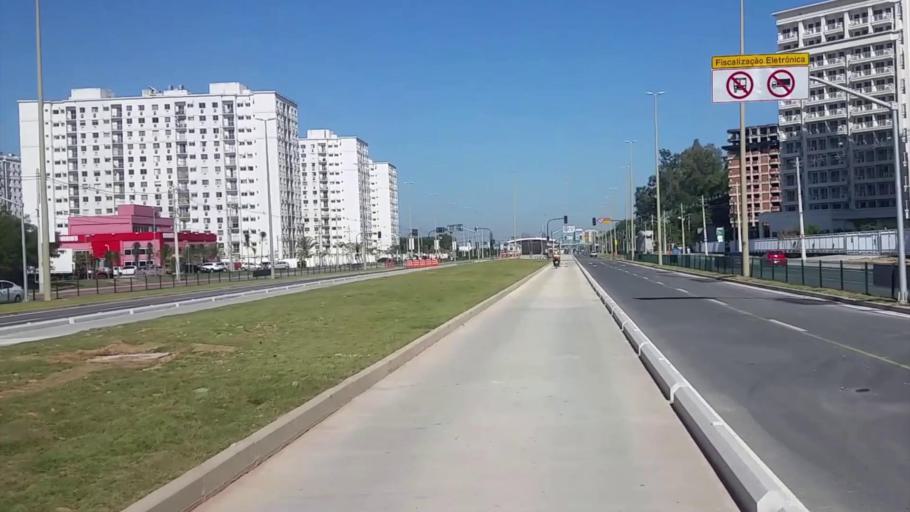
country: BR
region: Rio de Janeiro
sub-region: Nilopolis
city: Nilopolis
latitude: -22.9616
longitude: -43.3925
